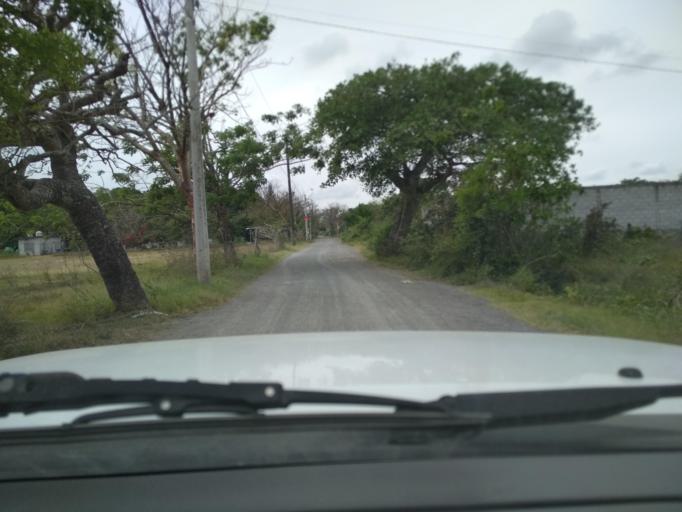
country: MX
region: Veracruz
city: El Tejar
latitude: 19.0636
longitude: -96.1364
